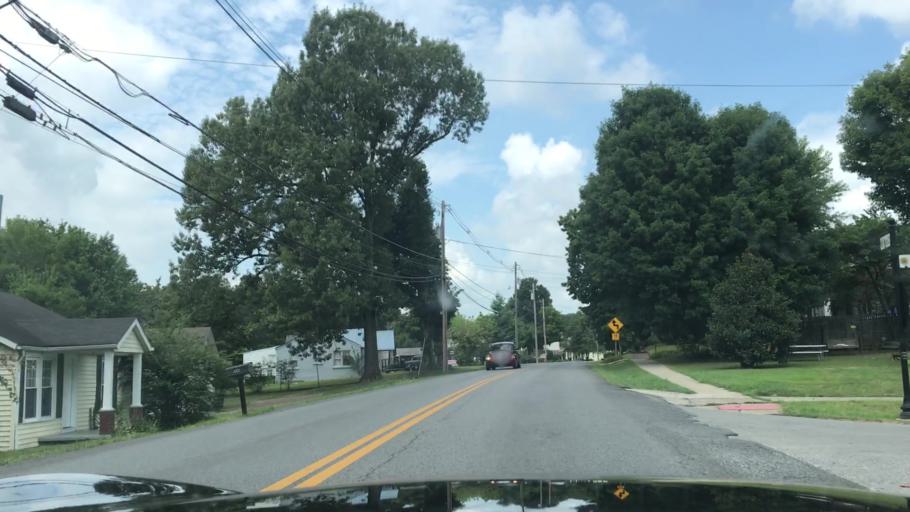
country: US
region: Kentucky
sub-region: Muhlenberg County
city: Greenville
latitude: 37.2049
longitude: -87.1682
